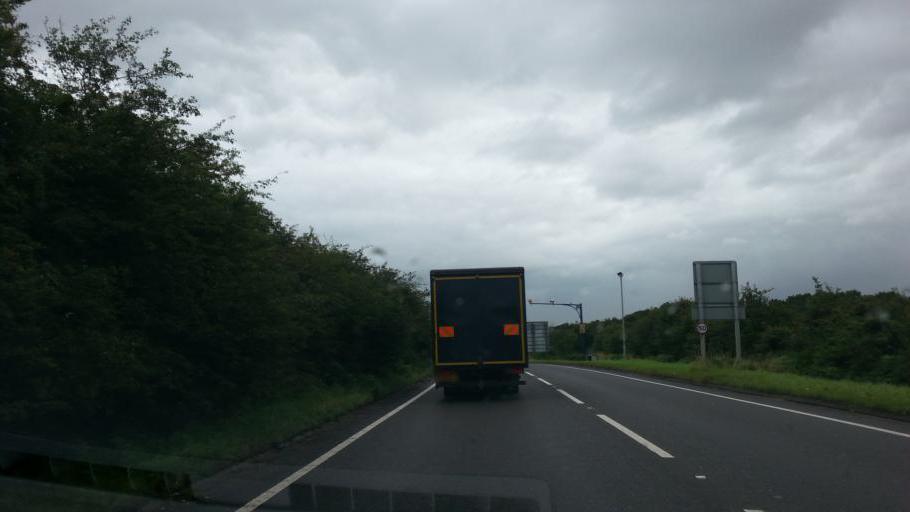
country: GB
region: England
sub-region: Nottinghamshire
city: Bilsthorpe
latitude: 53.1213
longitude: -1.0611
